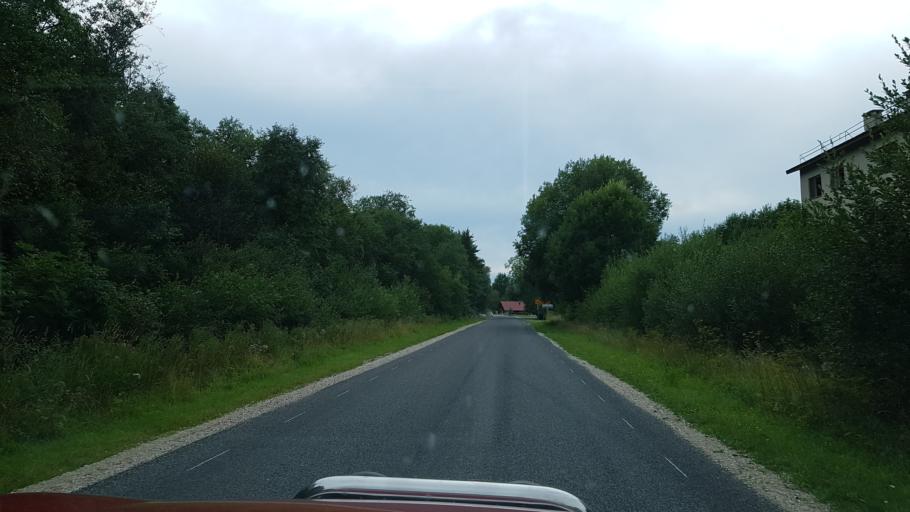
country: EE
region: Laeaene
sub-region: Lihula vald
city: Lihula
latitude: 58.8554
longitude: 23.8055
